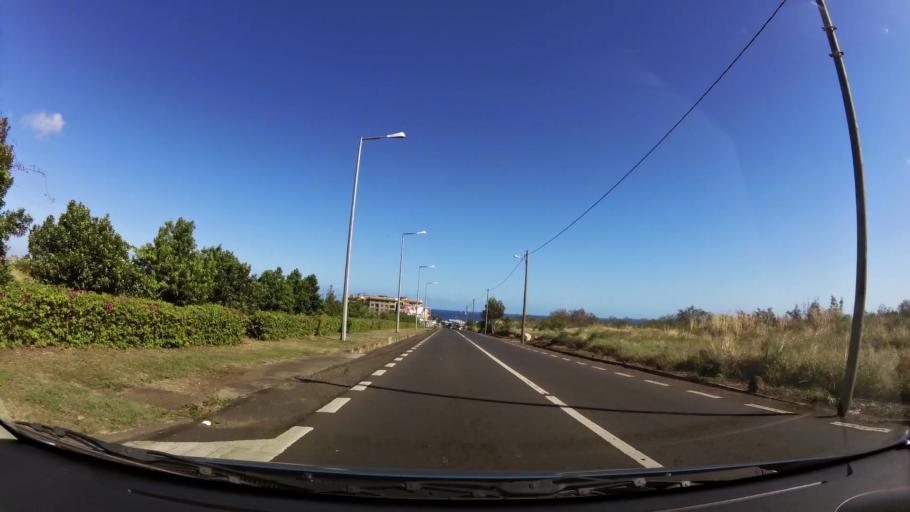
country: MU
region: Black River
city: Flic en Flac
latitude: -20.2768
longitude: 57.3813
